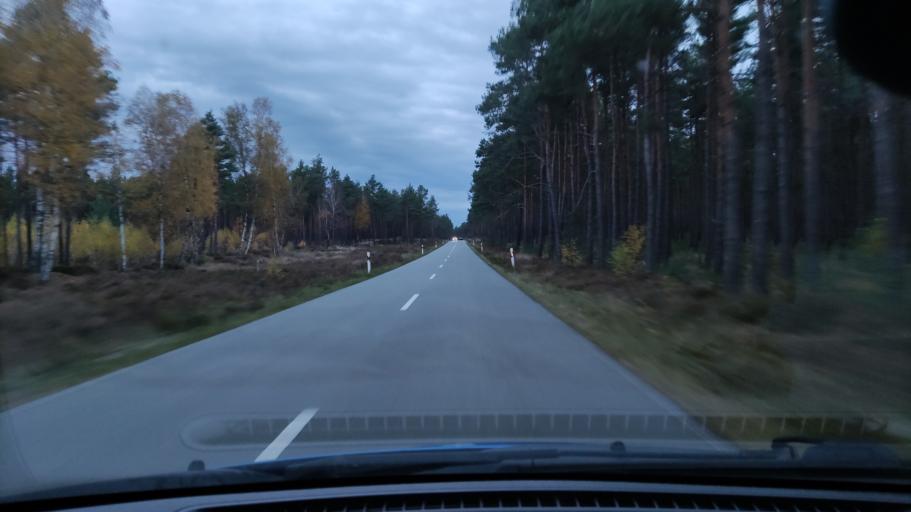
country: DE
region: Lower Saxony
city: Prezelle
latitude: 52.9793
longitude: 11.3980
